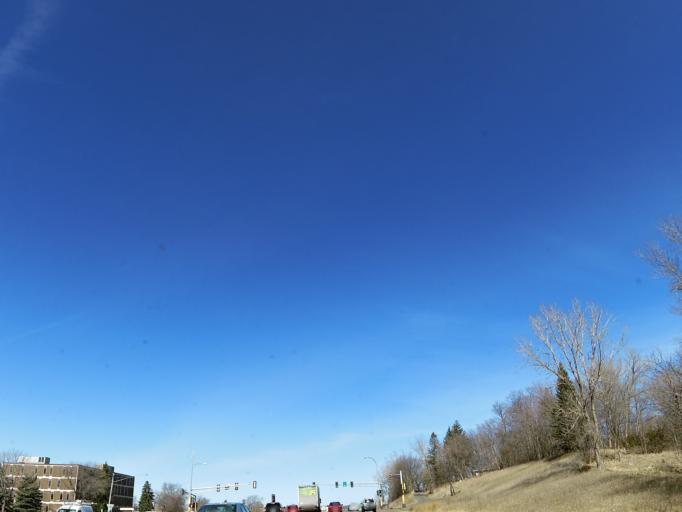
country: US
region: Minnesota
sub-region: Hennepin County
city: Plymouth
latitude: 44.9986
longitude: -93.4411
